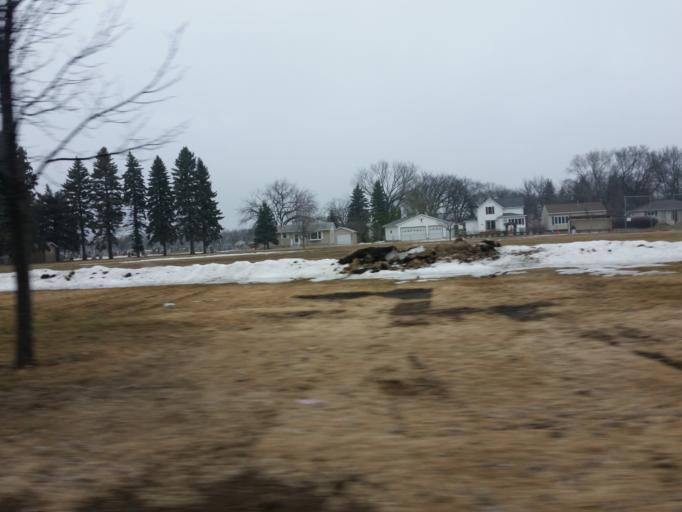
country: US
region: North Dakota
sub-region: Walsh County
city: Grafton
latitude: 48.4156
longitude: -97.4193
